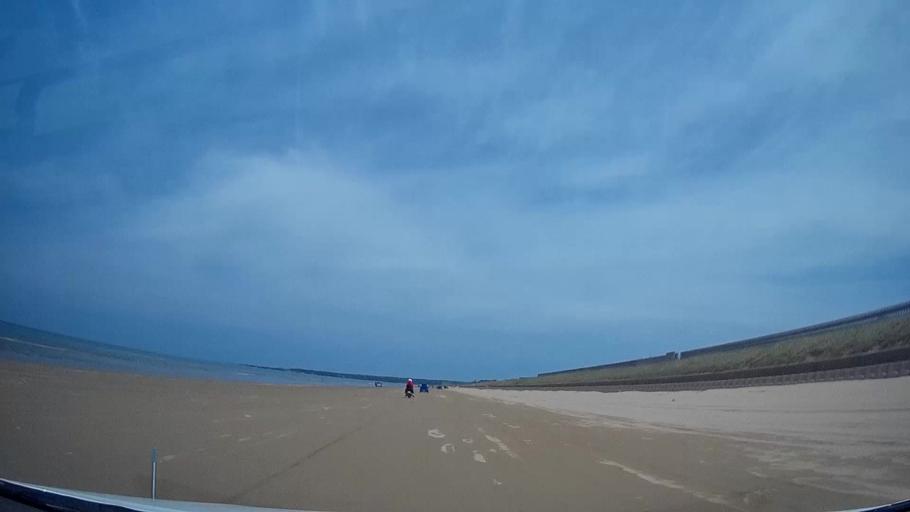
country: JP
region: Ishikawa
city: Hakui
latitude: 36.8758
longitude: 136.7612
